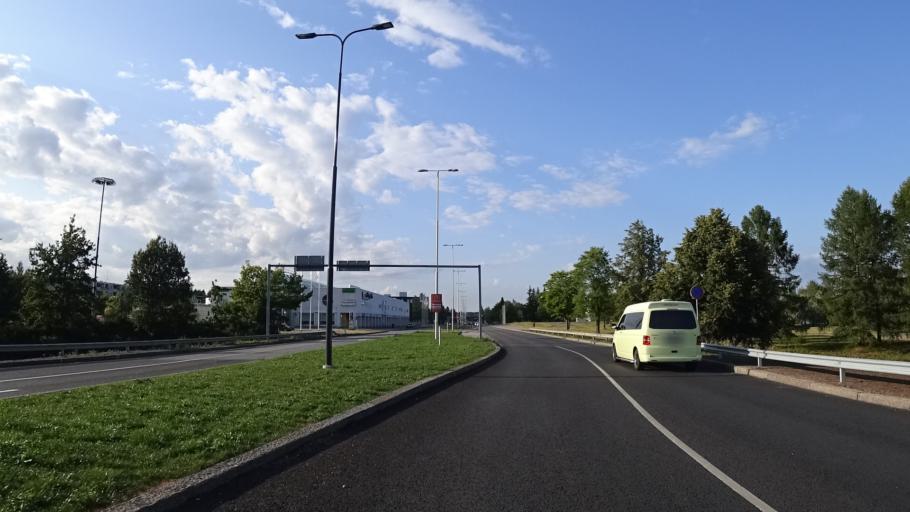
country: FI
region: South Karelia
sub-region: Imatra
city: Imatra
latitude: 61.1888
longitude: 28.7774
